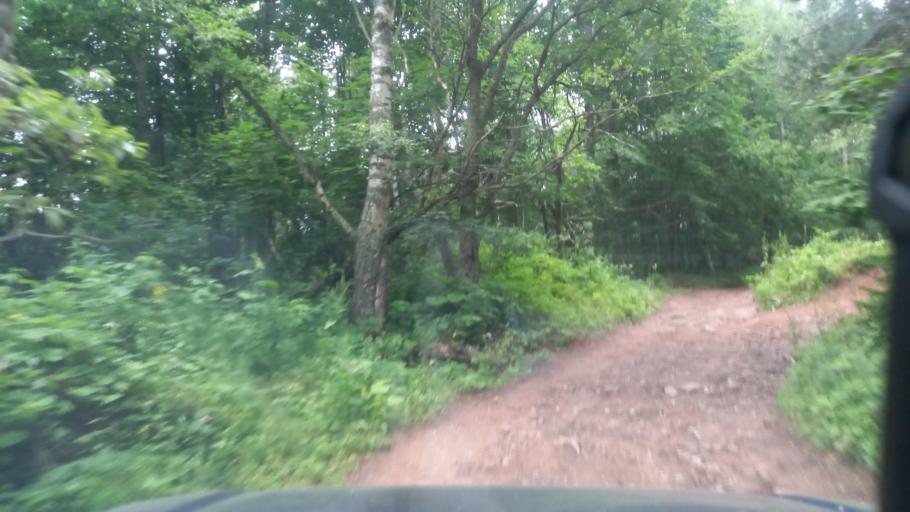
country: RU
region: Karachayevo-Cherkesiya
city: Kurdzhinovo
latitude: 43.8068
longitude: 40.8539
